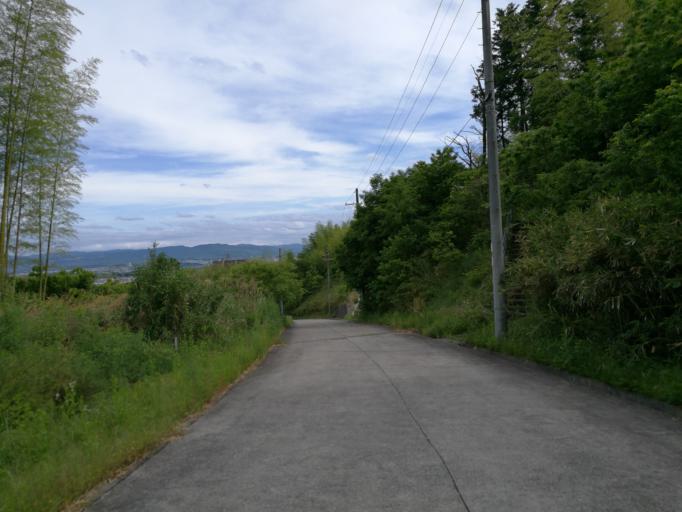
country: JP
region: Kyoto
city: Tanabe
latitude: 34.7677
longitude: 135.7803
